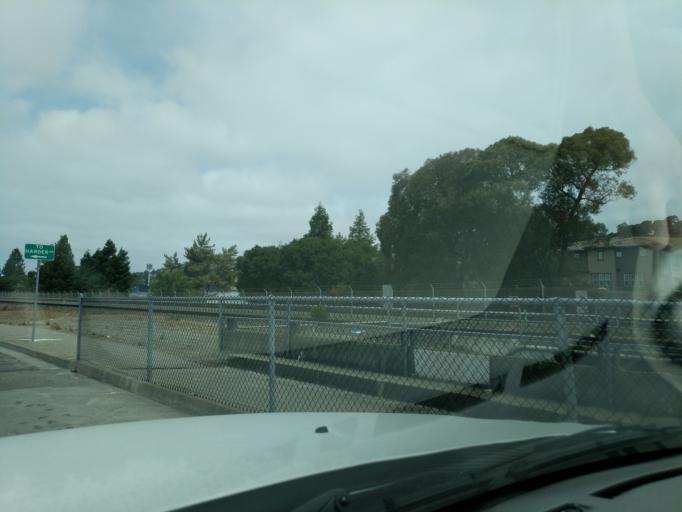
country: US
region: California
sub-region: Alameda County
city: Hayward
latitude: 37.6505
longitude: -122.0704
